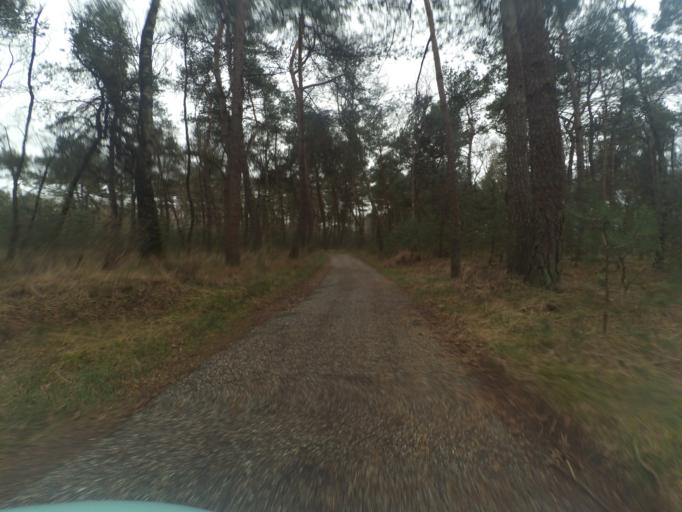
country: NL
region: Gelderland
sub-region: Gemeente Arnhem
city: Gulden Bodem
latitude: 52.0236
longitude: 5.9108
